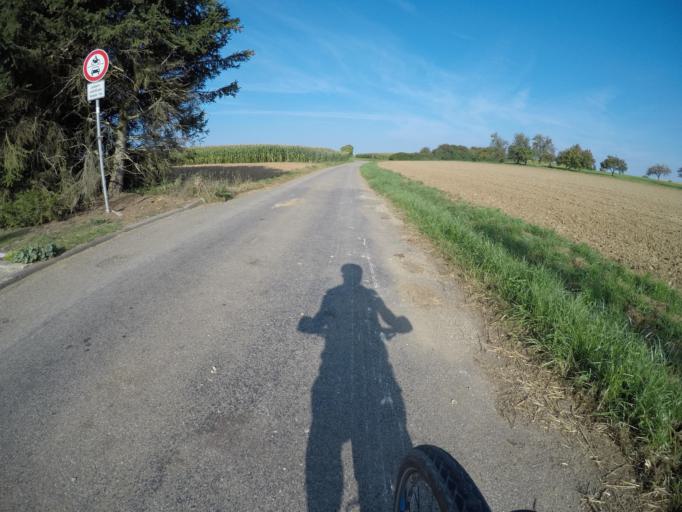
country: DE
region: Baden-Wuerttemberg
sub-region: Regierungsbezirk Stuttgart
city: Gerstetten
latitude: 48.6072
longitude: 10.0657
